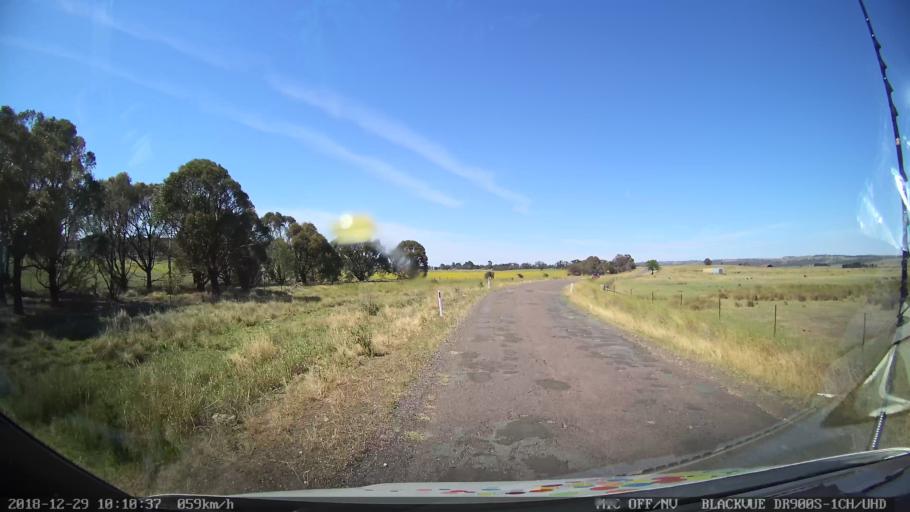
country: AU
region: New South Wales
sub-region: Yass Valley
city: Gundaroo
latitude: -34.8774
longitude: 149.4561
